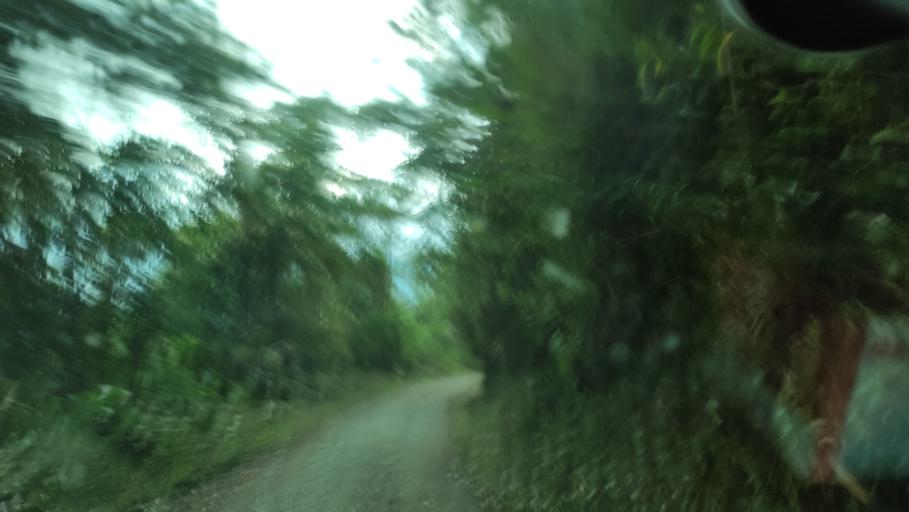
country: CO
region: Valle del Cauca
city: San Pedro
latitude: 3.8820
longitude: -76.1559
